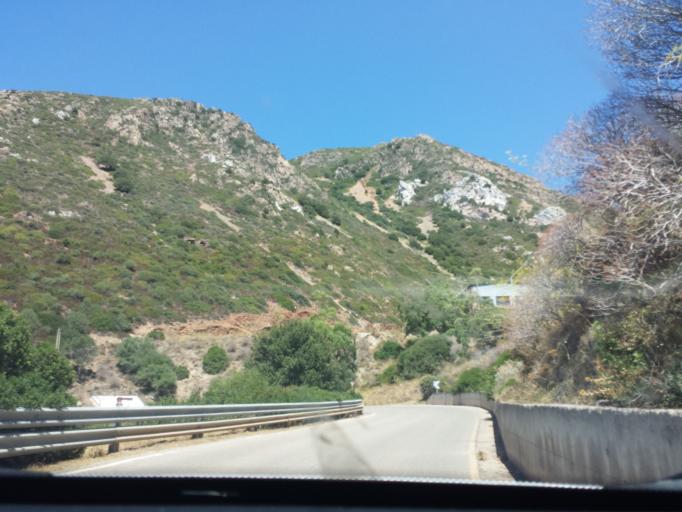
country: IT
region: Sardinia
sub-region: Provincia di Carbonia-Iglesias
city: Gonnesa
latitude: 39.3232
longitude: 8.4362
